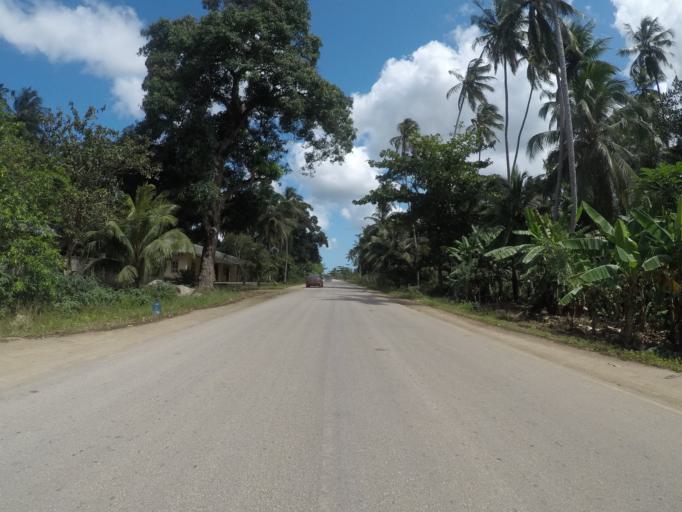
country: TZ
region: Zanzibar Central/South
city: Koani
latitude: -6.1537
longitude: 39.3296
